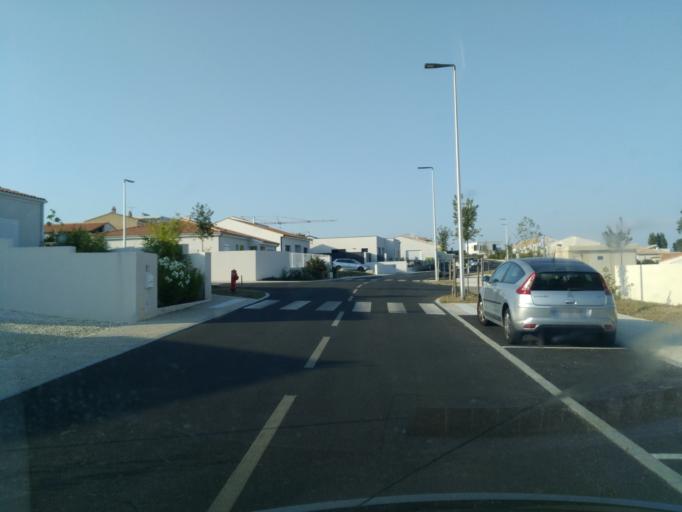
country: FR
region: Poitou-Charentes
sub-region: Departement de la Charente-Maritime
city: Vaux-sur-Mer
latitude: 45.6384
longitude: -1.0554
